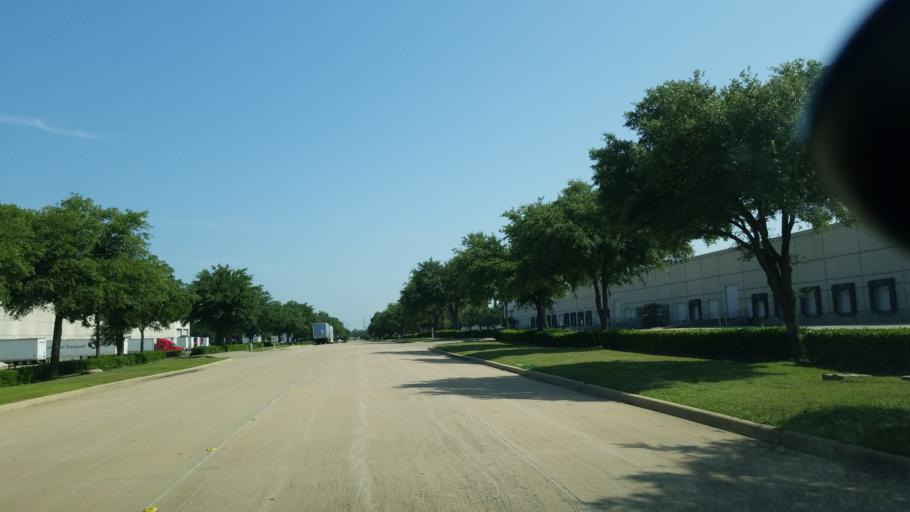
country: US
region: Texas
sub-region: Dallas County
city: Coppell
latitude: 32.9410
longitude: -96.9985
